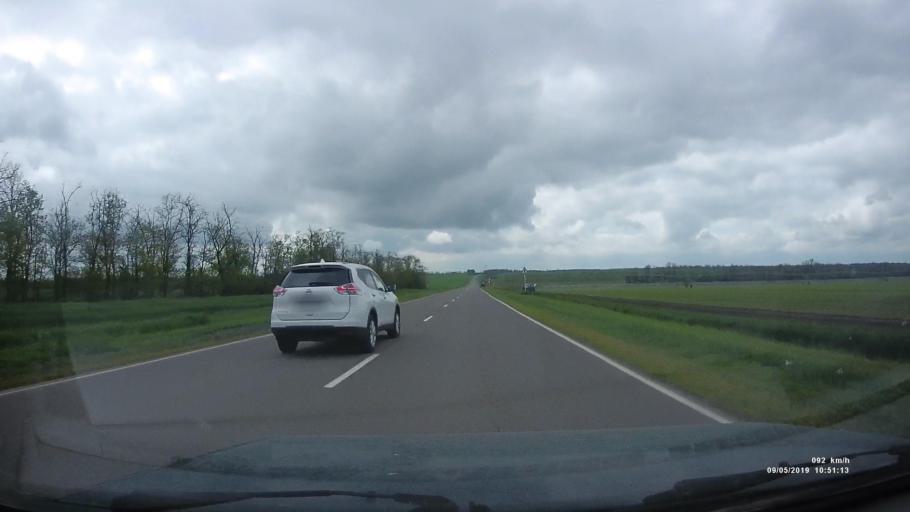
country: RU
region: Rostov
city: Peshkovo
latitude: 46.9179
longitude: 39.3552
